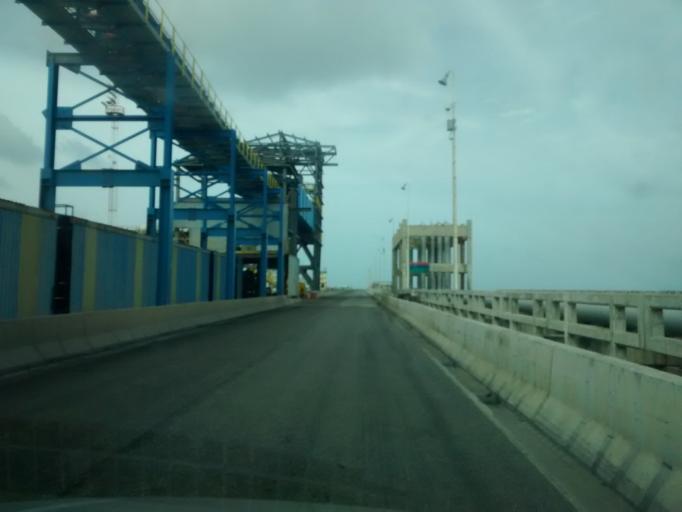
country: BR
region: Ceara
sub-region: Caucaia
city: Cambebba
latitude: -3.5358
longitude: -38.7988
